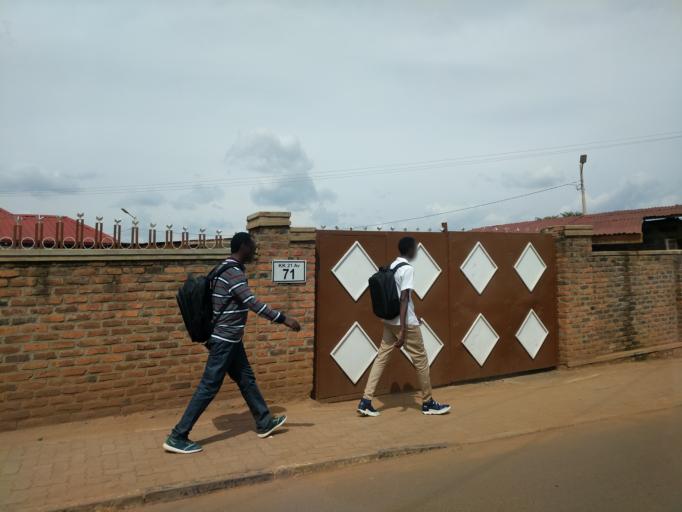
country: RW
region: Kigali
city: Kigali
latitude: -1.9804
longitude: 30.1157
